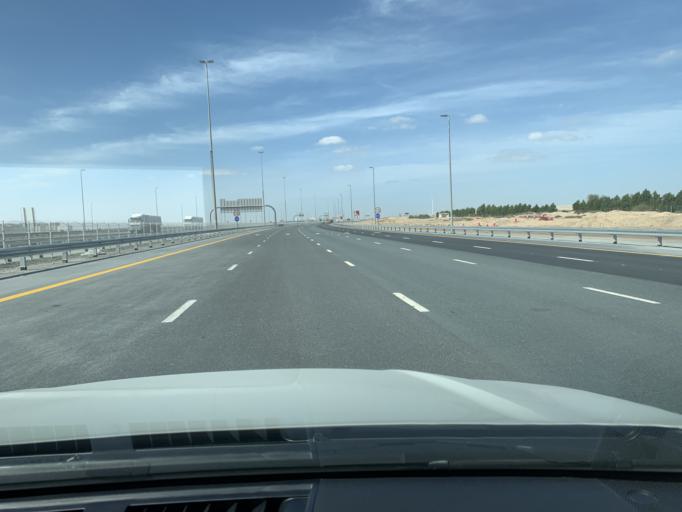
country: AE
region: Dubai
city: Dubai
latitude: 24.9552
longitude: 55.2214
